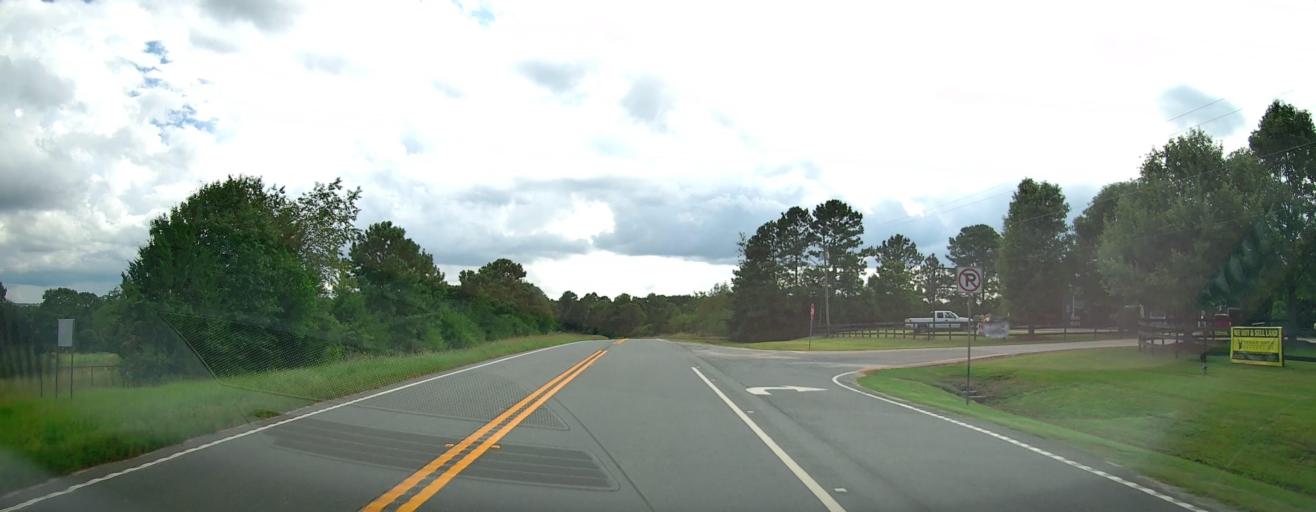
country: US
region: Georgia
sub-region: Meriwether County
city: Manchester
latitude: 32.9807
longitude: -84.5967
